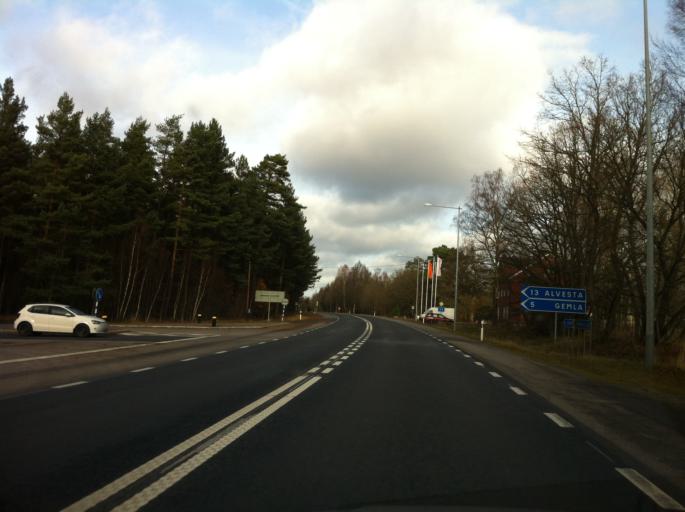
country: SE
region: Kronoberg
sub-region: Vaxjo Kommun
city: Gemla
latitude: 56.7930
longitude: 14.6286
